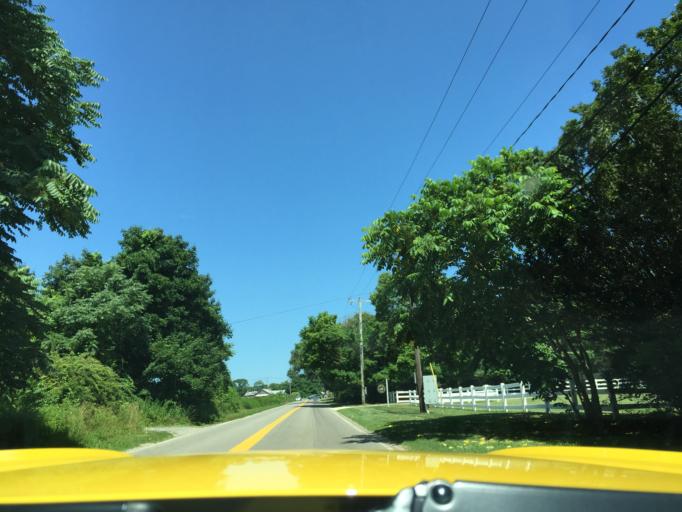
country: US
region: New York
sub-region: Suffolk County
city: Bridgehampton
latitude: 40.9425
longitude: -72.2609
